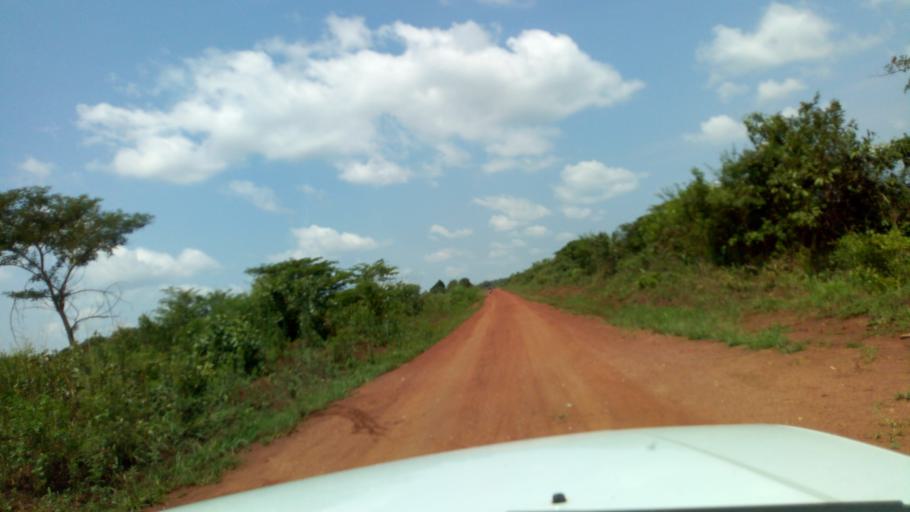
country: UG
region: Western Region
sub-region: Masindi District
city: Masindi
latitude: 1.7345
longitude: 31.8807
